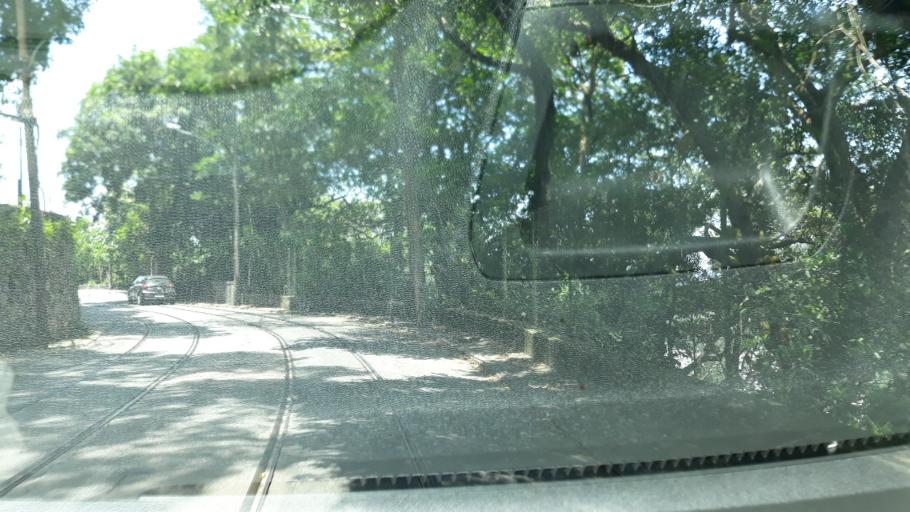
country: BR
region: Rio de Janeiro
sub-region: Rio De Janeiro
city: Rio de Janeiro
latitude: -22.9376
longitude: -43.2044
